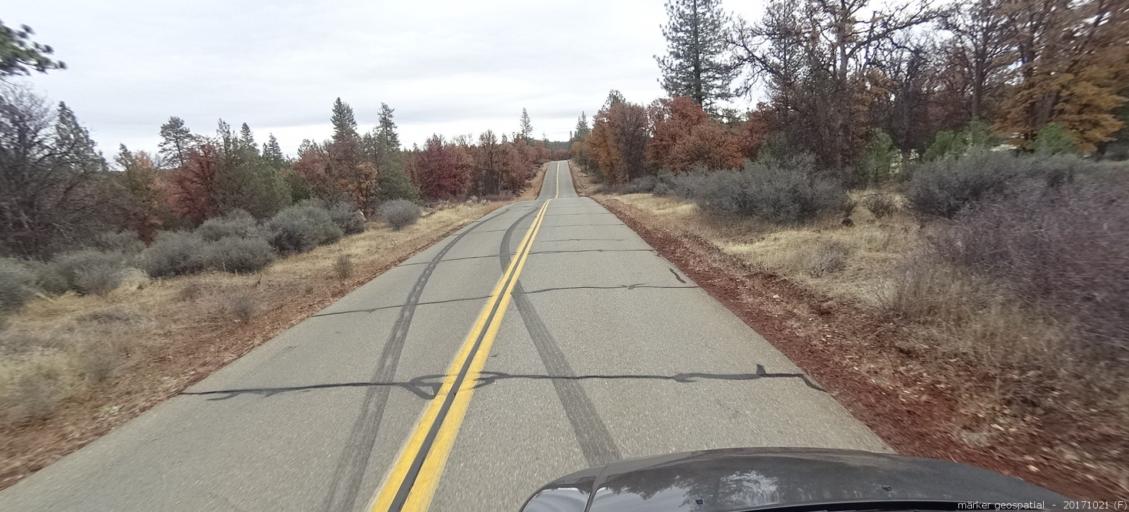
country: US
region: California
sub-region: Shasta County
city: Burney
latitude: 40.9326
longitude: -121.5618
